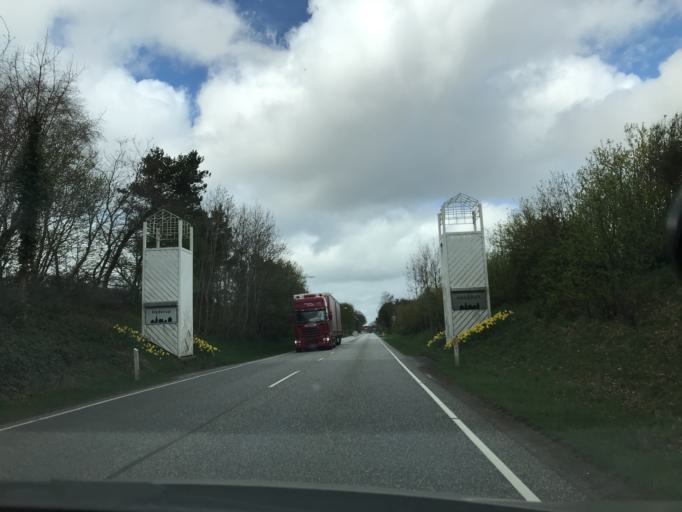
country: DK
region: Central Jutland
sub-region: Herning Kommune
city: Sunds
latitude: 56.3831
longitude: 8.9902
